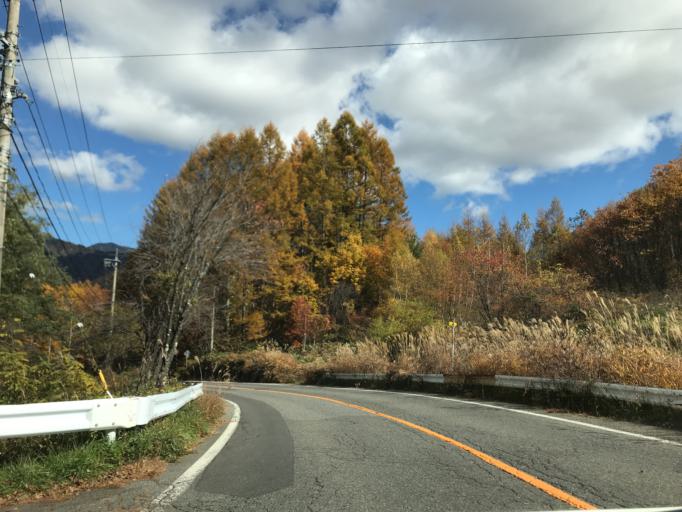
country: JP
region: Nagano
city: Toyoshina
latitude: 36.1311
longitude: 137.6623
